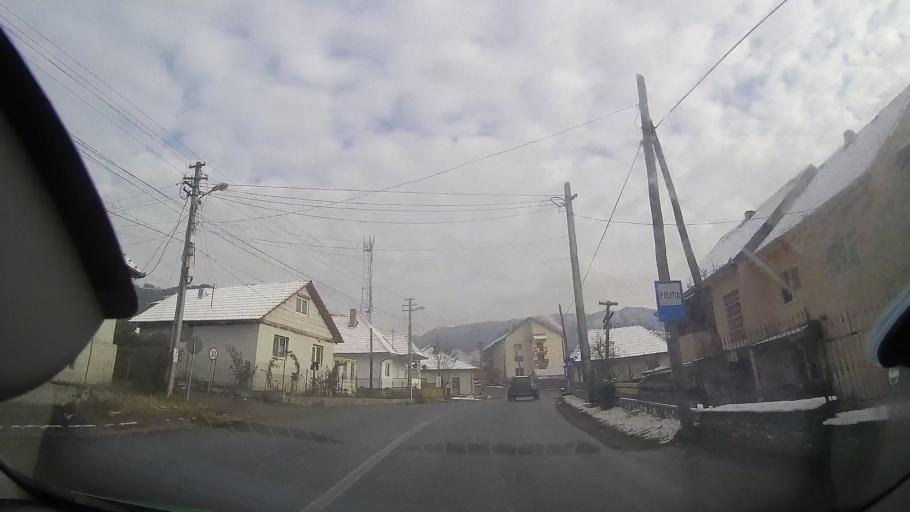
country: RO
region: Alba
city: Salciua de Sus
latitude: 46.3977
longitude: 23.4160
